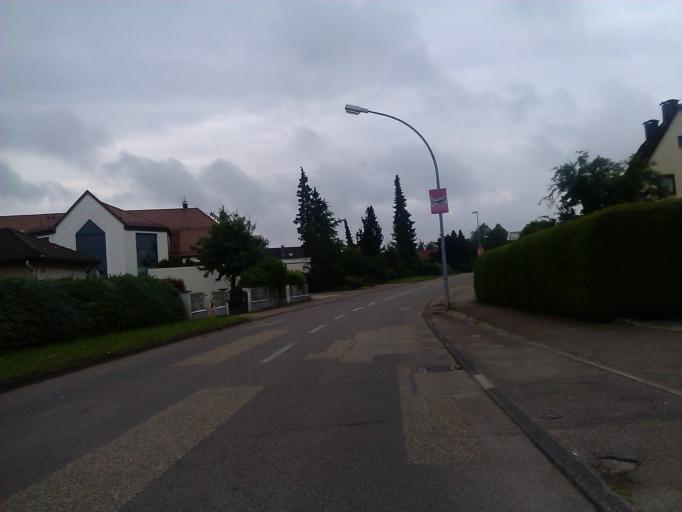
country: DE
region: Baden-Wuerttemberg
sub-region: Regierungsbezirk Stuttgart
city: Mainhardt
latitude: 49.0728
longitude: 9.5575
